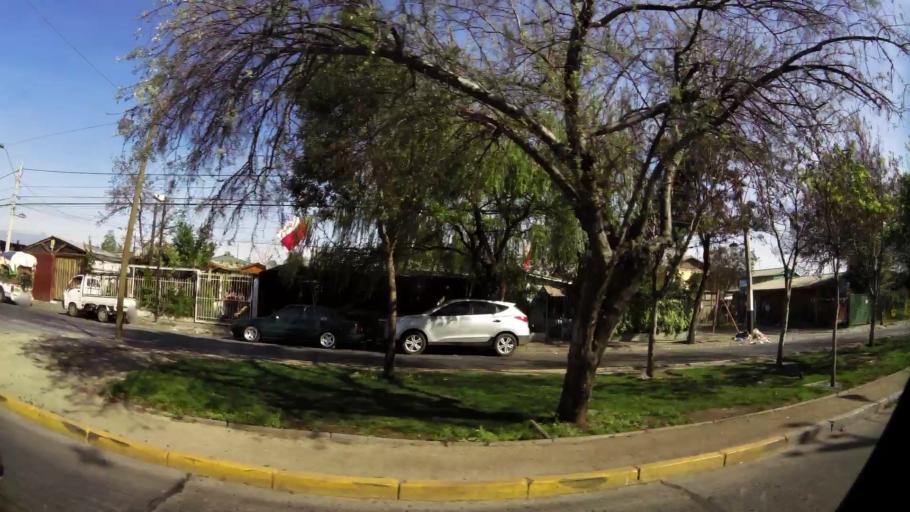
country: CL
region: Santiago Metropolitan
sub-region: Provincia de Santiago
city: La Pintana
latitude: -33.5374
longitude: -70.6334
